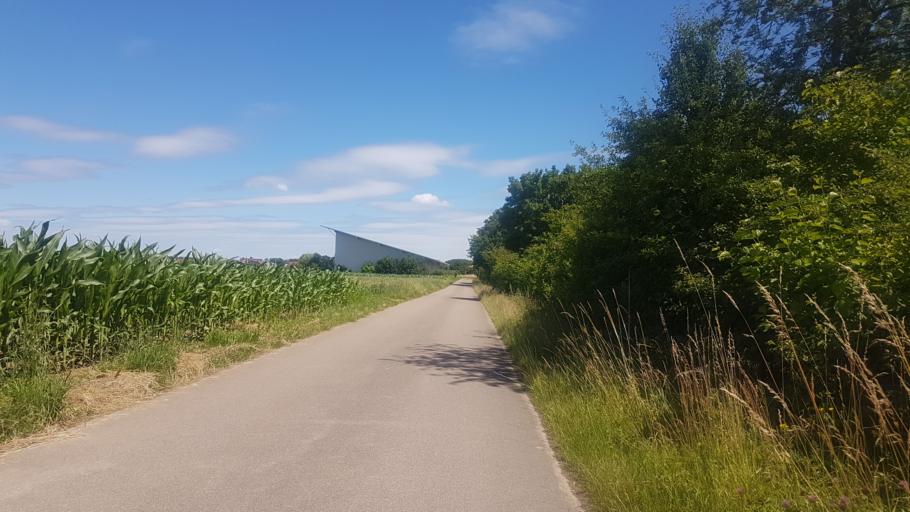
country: DE
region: Bavaria
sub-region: Swabia
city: Blindheim
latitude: 48.6355
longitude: 10.6312
